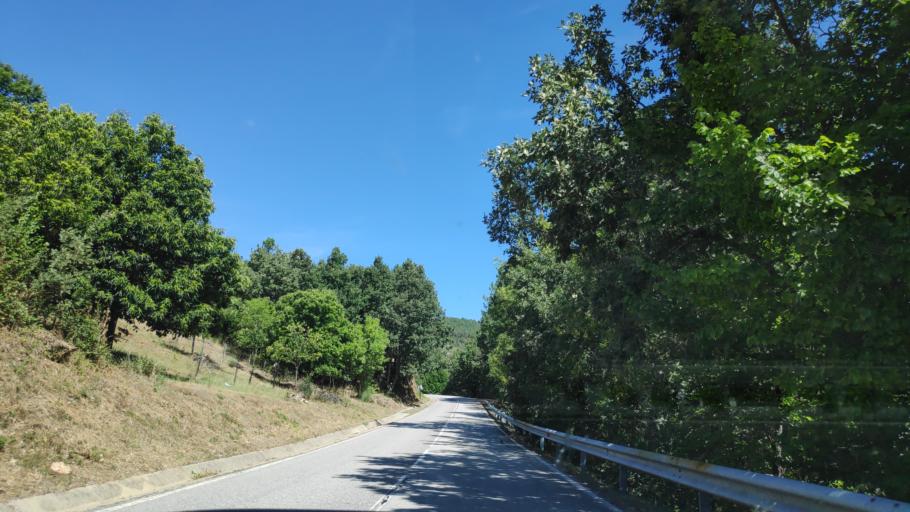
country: PT
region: Braganca
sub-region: Braganca Municipality
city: Braganca
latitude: 41.9126
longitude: -6.7291
